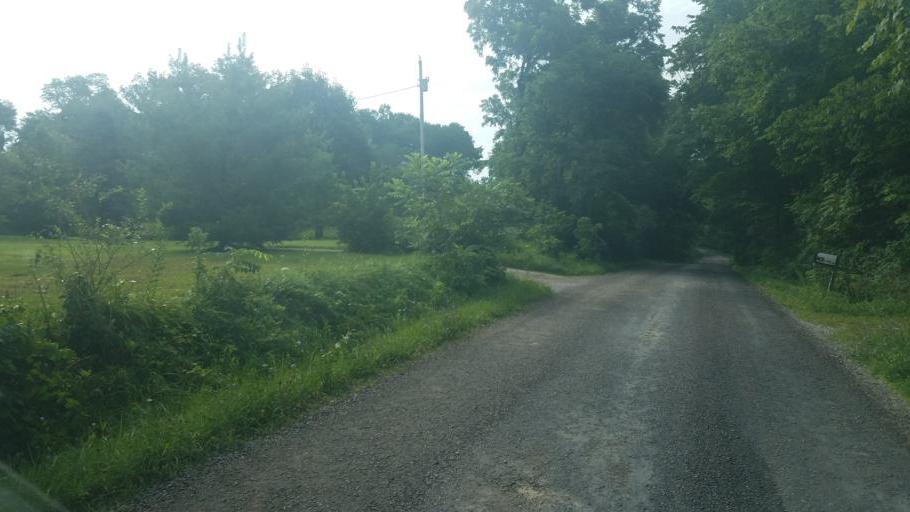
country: US
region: Ohio
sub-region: Delaware County
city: Ashley
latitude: 40.3767
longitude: -82.8890
